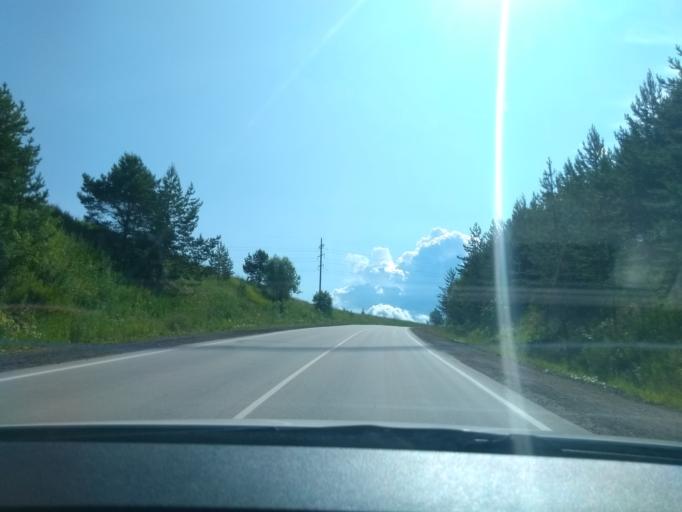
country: RU
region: Perm
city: Lobanovo
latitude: 57.8389
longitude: 56.3913
